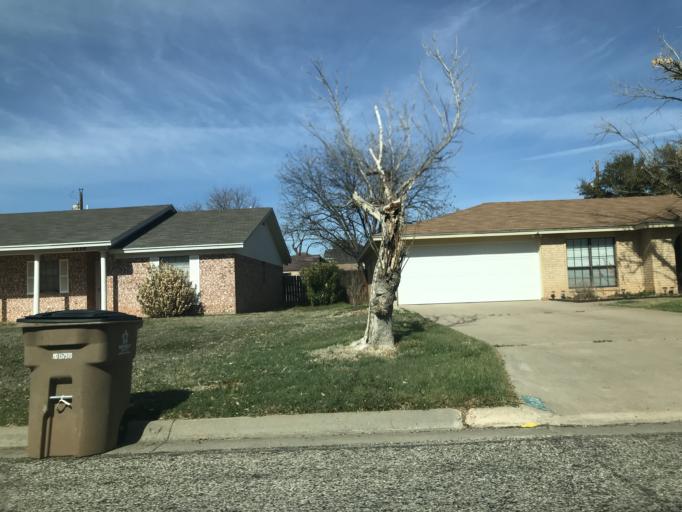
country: US
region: Texas
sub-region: Tom Green County
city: San Angelo
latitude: 31.4372
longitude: -100.4838
